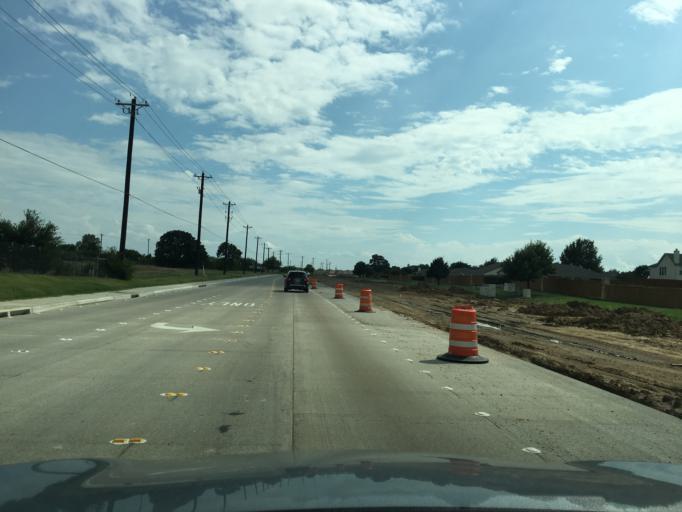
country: US
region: Texas
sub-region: Denton County
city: Oak Point
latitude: 33.2068
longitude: -96.9758
